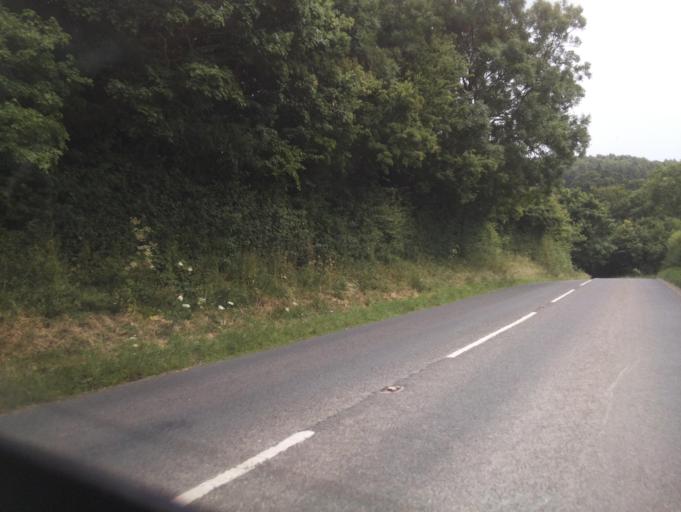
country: GB
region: England
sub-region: Devon
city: Colyton
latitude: 50.7237
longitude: -3.0478
